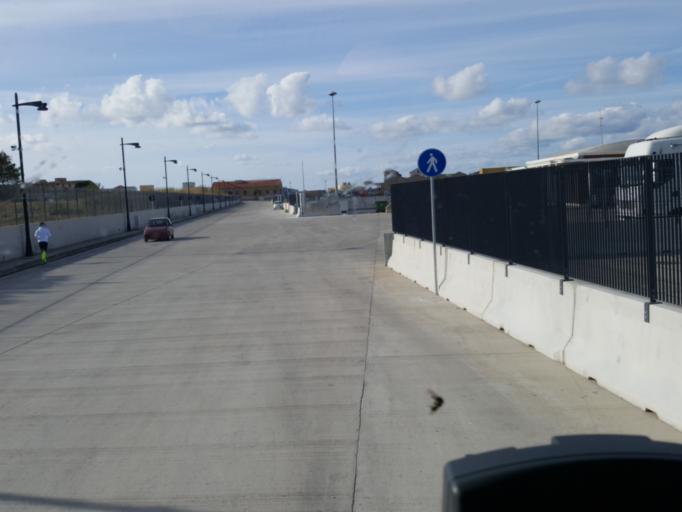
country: IT
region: Sicily
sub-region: Palermo
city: Termini Imerese
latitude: 37.9868
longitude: 13.7028
